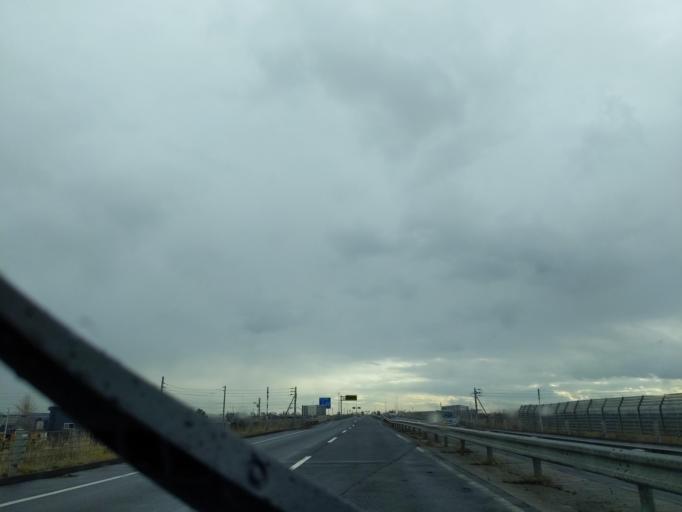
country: JP
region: Hokkaido
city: Ebetsu
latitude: 43.1422
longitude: 141.5666
